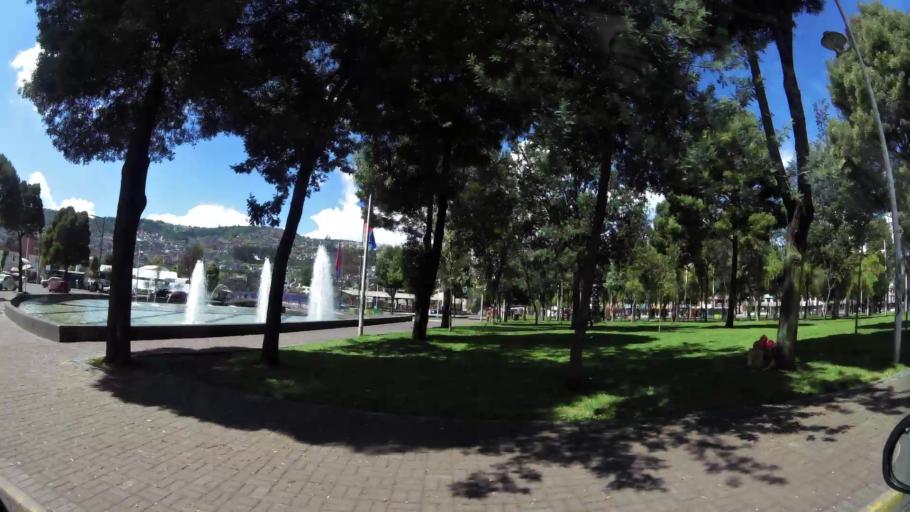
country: EC
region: Pichincha
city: Quito
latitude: -0.2726
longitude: -78.5374
